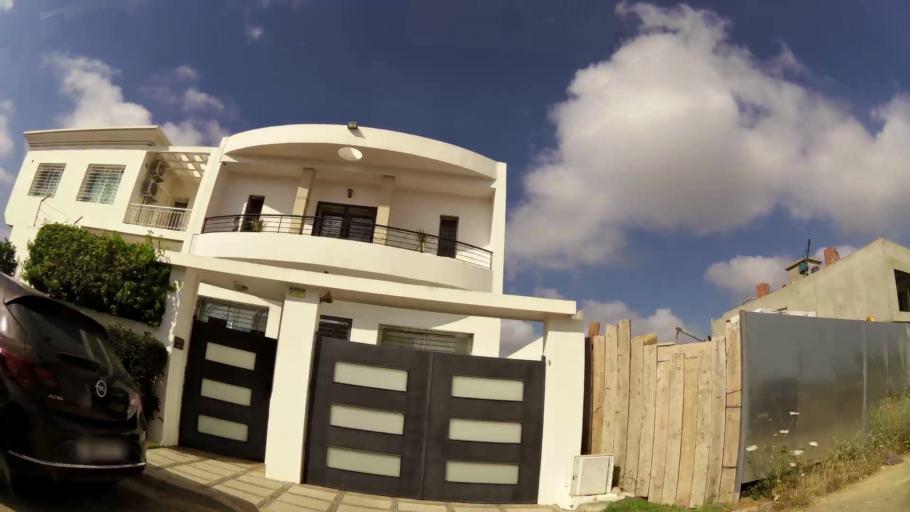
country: MA
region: Rabat-Sale-Zemmour-Zaer
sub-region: Skhirate-Temara
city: Temara
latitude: 33.9504
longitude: -6.8806
